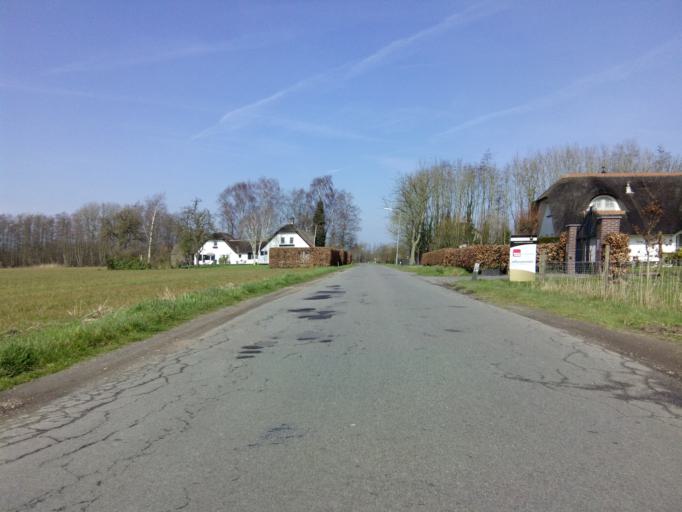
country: NL
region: Gelderland
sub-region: Gemeente Barneveld
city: Zwartebroek
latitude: 52.1804
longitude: 5.5091
